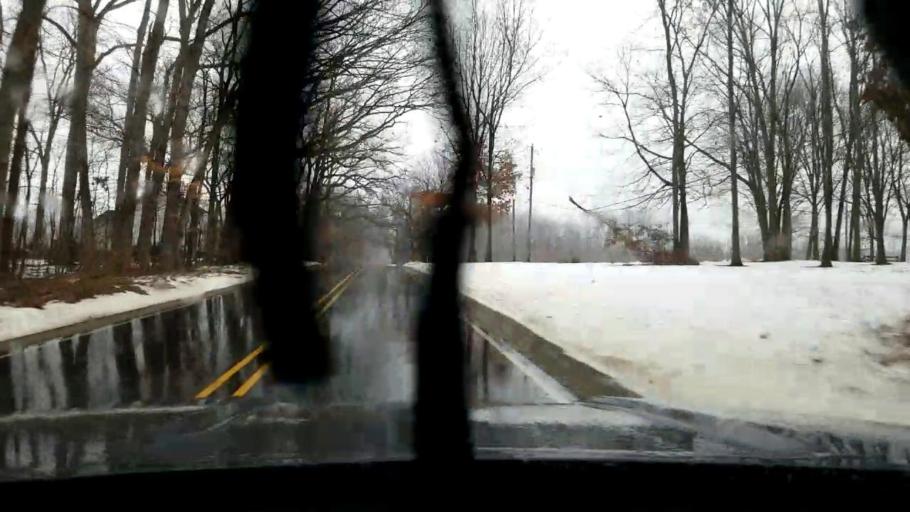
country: US
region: Michigan
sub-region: Jackson County
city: Michigan Center
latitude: 42.3212
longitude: -84.2937
